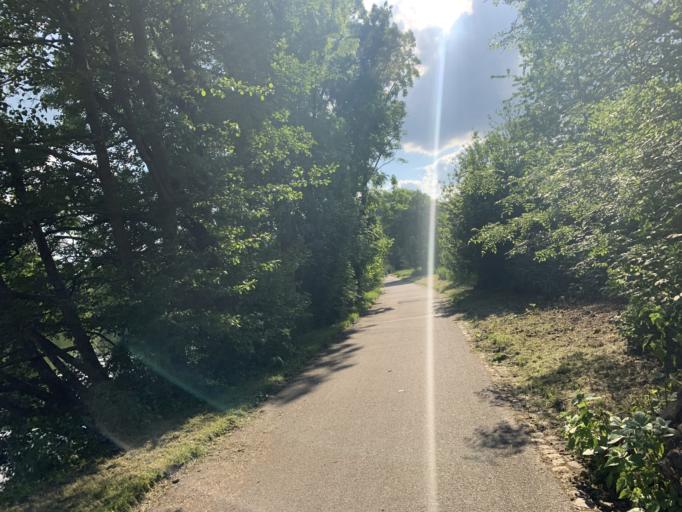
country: DE
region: North Rhine-Westphalia
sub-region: Regierungsbezirk Dusseldorf
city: Heiligenhaus
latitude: 51.3769
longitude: 6.9700
